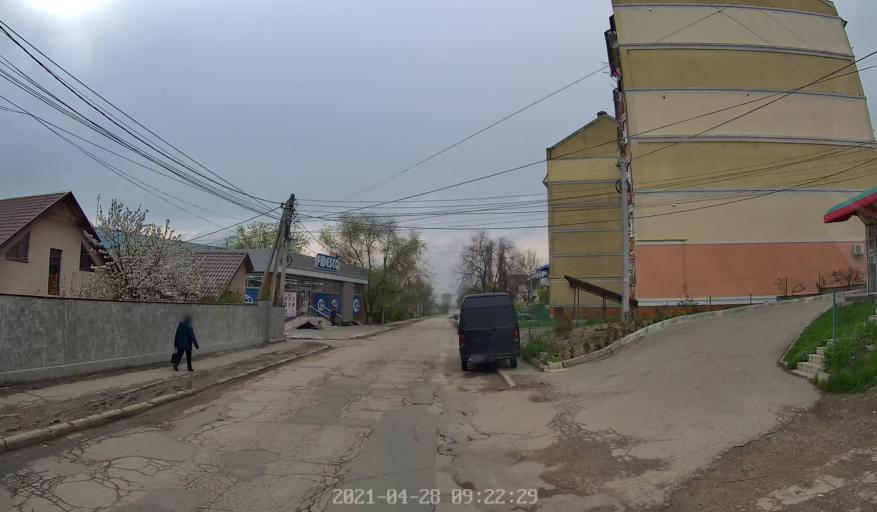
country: MD
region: Chisinau
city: Singera
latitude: 46.9836
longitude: 28.9329
